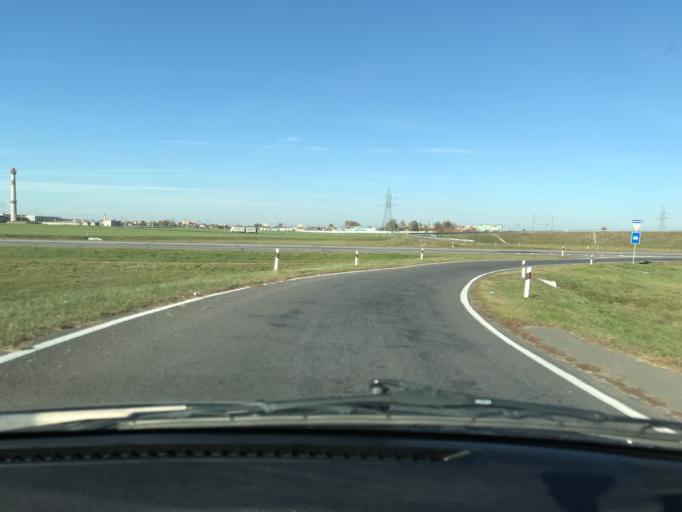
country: BY
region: Brest
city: Ivatsevichy
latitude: 52.6979
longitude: 25.3615
